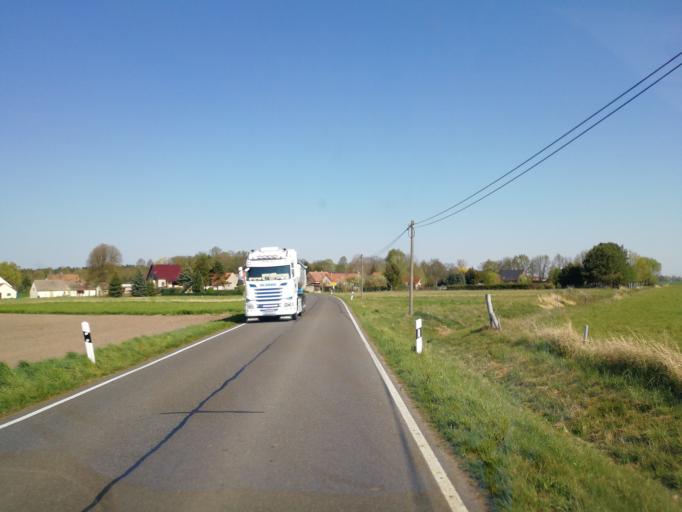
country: DE
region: Brandenburg
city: Crinitz
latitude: 51.7355
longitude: 13.8515
